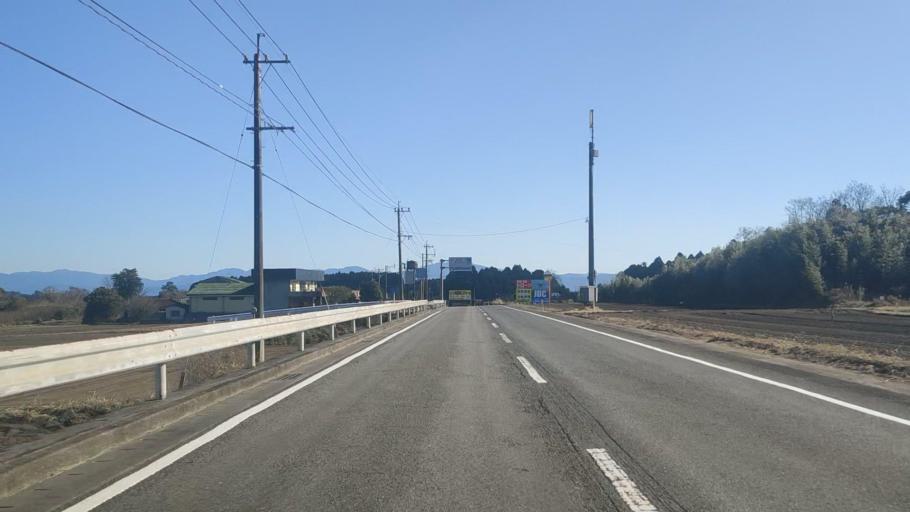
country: JP
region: Kagoshima
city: Sueyoshicho-ninokata
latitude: 31.6882
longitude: 130.9587
